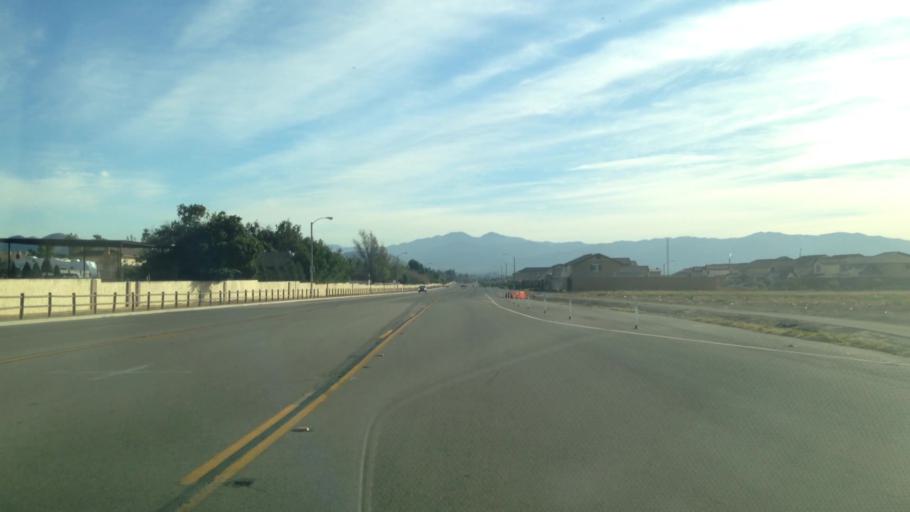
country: US
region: California
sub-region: Riverside County
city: Mira Loma
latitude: 33.9909
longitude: -117.5407
